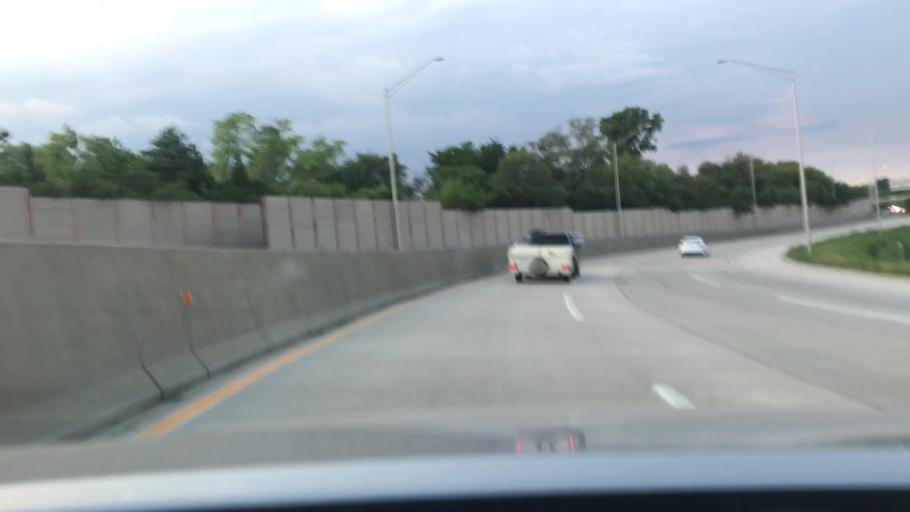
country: US
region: Illinois
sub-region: Cook County
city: Indian Head Park
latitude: 41.7667
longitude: -87.9085
